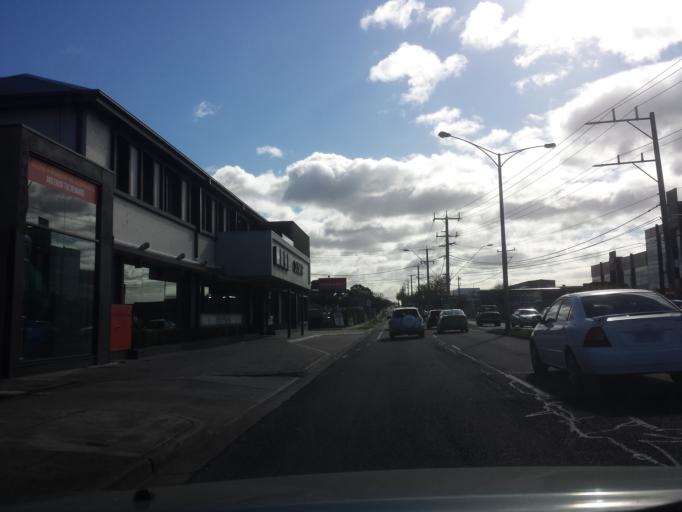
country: AU
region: Victoria
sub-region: Darebin
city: Preston
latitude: -37.7469
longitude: 145.0218
